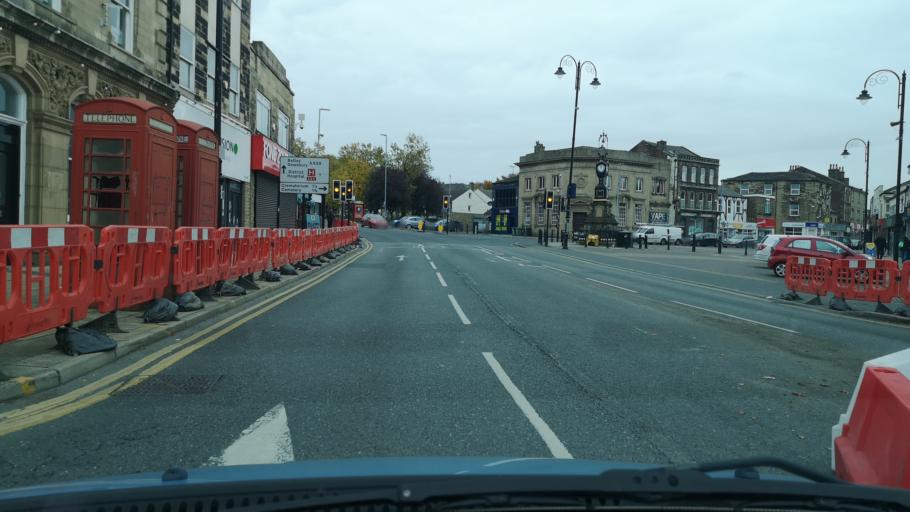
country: GB
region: England
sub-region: Kirklees
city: Heckmondwike
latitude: 53.7074
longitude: -1.6751
